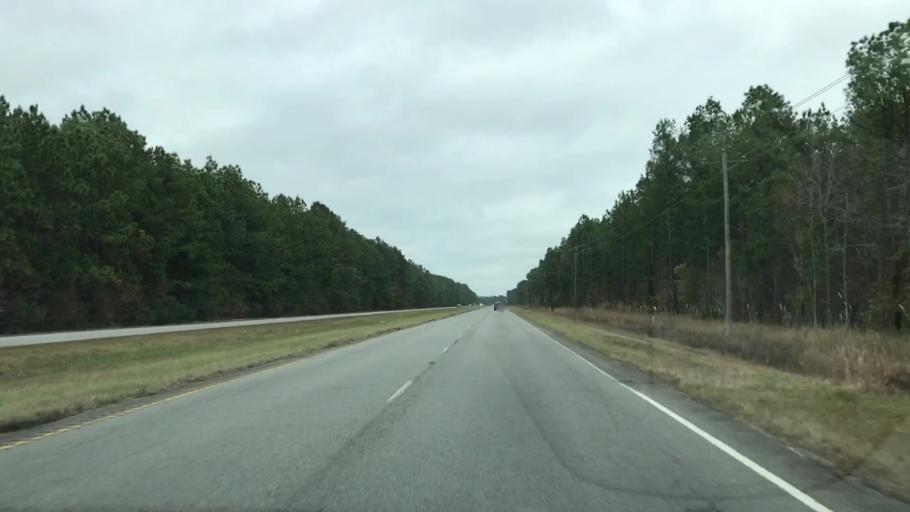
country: US
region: South Carolina
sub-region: Charleston County
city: Awendaw
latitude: 33.0149
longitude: -79.6356
